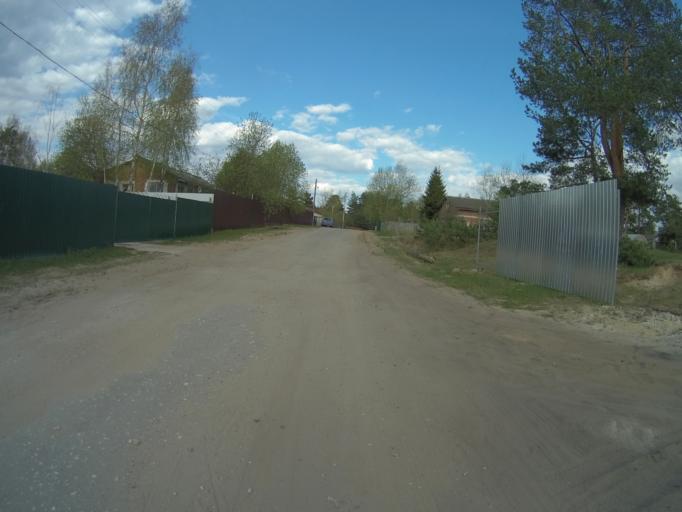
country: RU
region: Vladimir
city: Raduzhnyy
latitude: 56.0321
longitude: 40.3886
